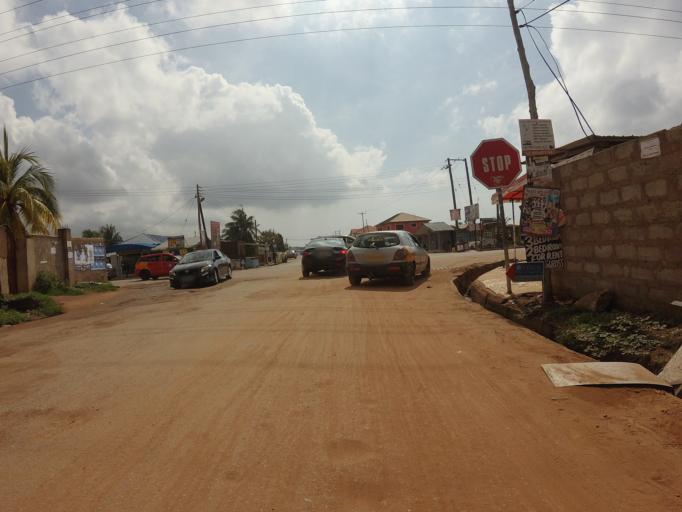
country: GH
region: Greater Accra
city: Nungua
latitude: 5.6190
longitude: -0.0929
